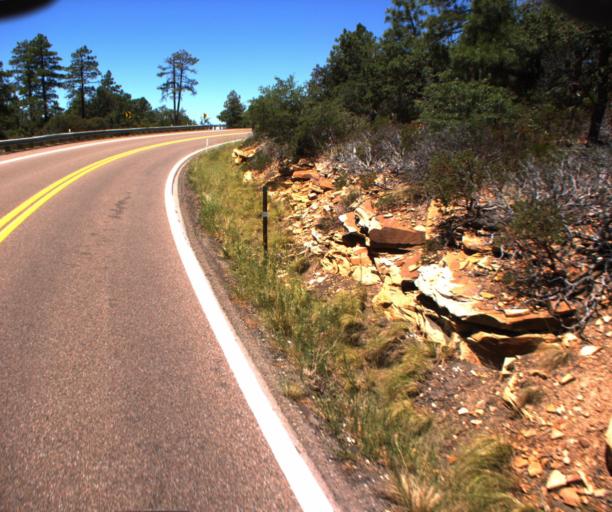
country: US
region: Arizona
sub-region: Gila County
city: Pine
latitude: 34.4213
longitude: -111.5106
